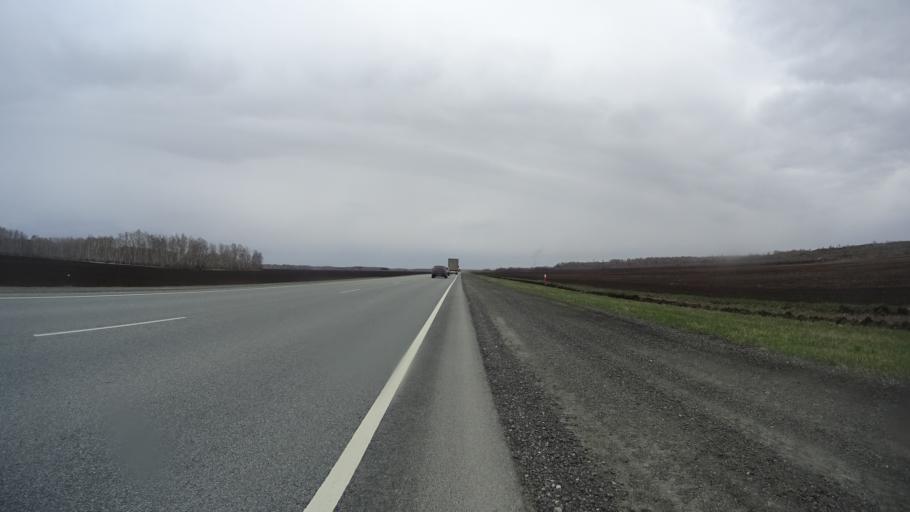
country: RU
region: Chelyabinsk
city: Krasnogorskiy
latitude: 54.5765
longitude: 61.2914
